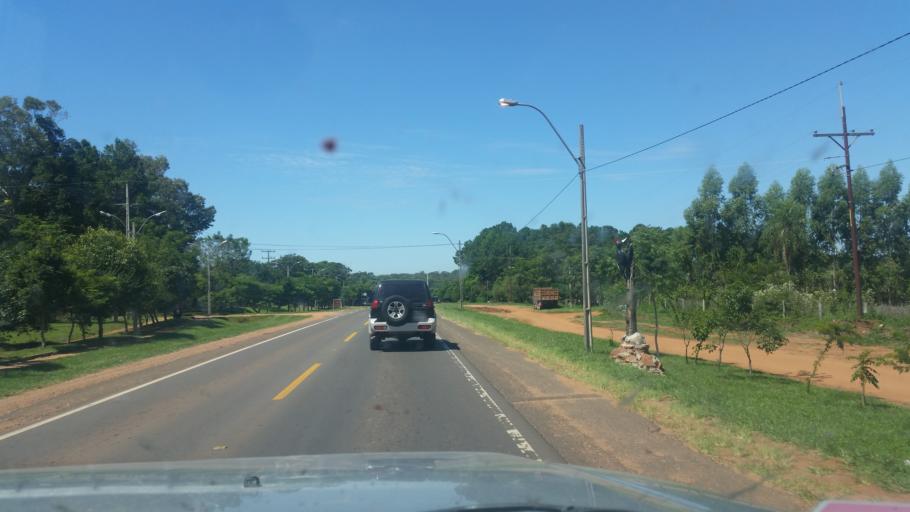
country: PY
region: Misiones
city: San Juan Bautista
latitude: -26.6735
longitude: -57.1165
